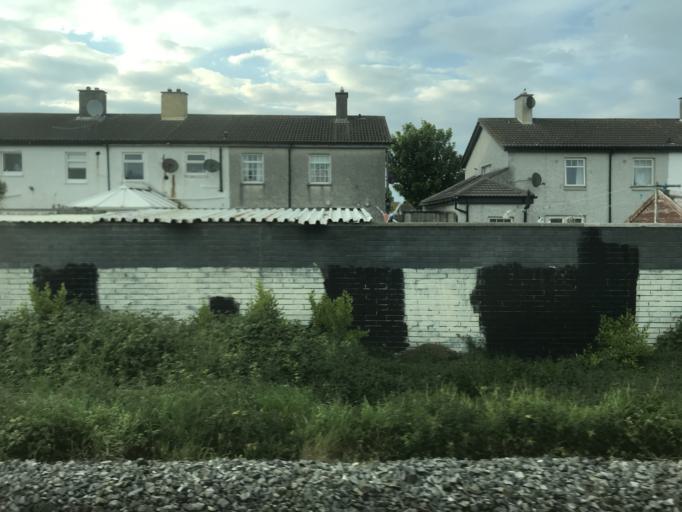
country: IE
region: Leinster
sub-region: Fingal County
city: Baldoyle
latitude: 53.3916
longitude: -6.1281
